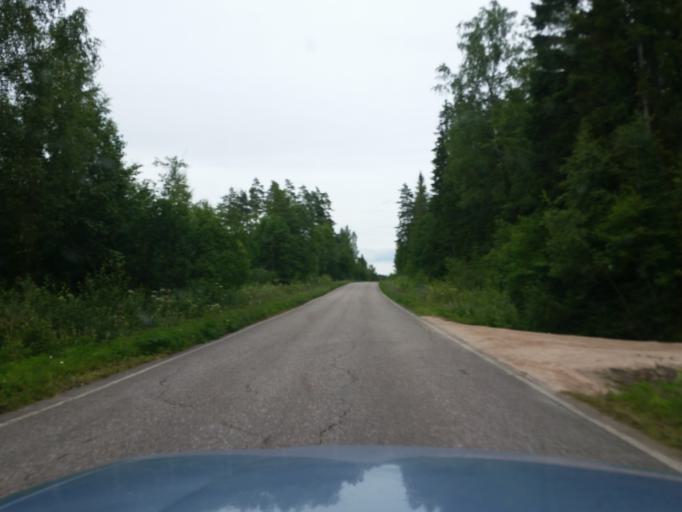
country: FI
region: Uusimaa
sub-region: Helsinki
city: Sammatti
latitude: 60.4311
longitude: 23.8269
